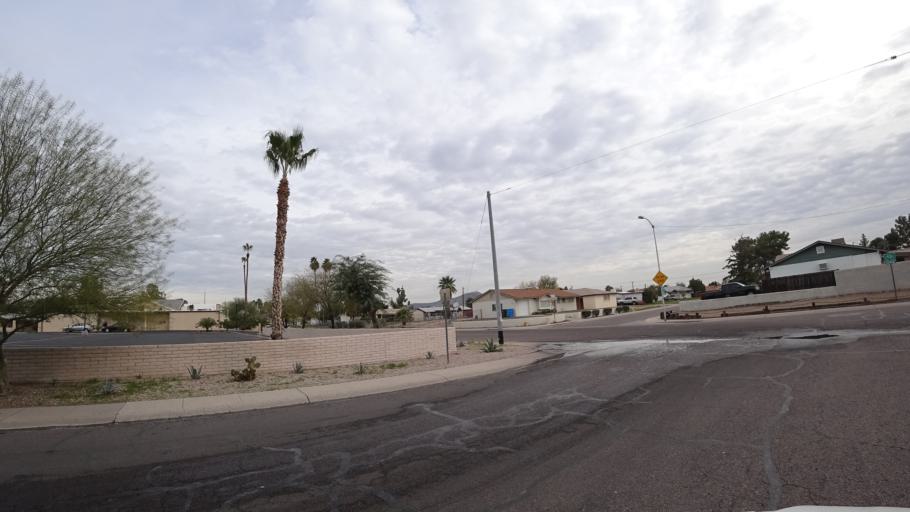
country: US
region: Arizona
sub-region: Maricopa County
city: Glendale
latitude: 33.6194
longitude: -112.1207
